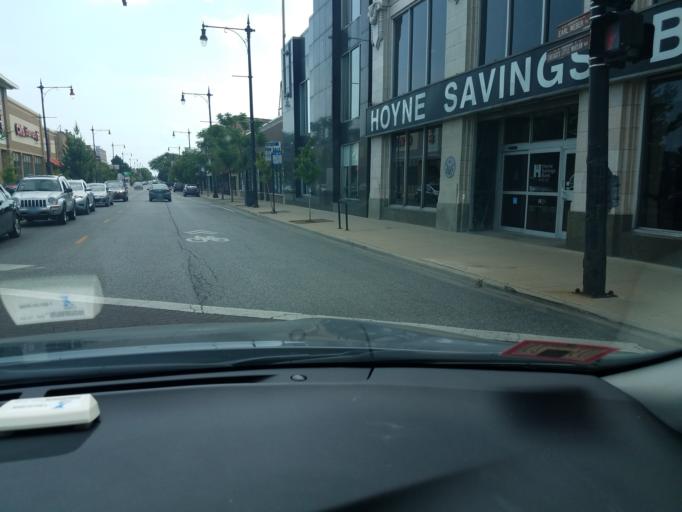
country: US
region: Illinois
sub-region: Cook County
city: Harwood Heights
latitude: 41.9678
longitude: -87.7608
